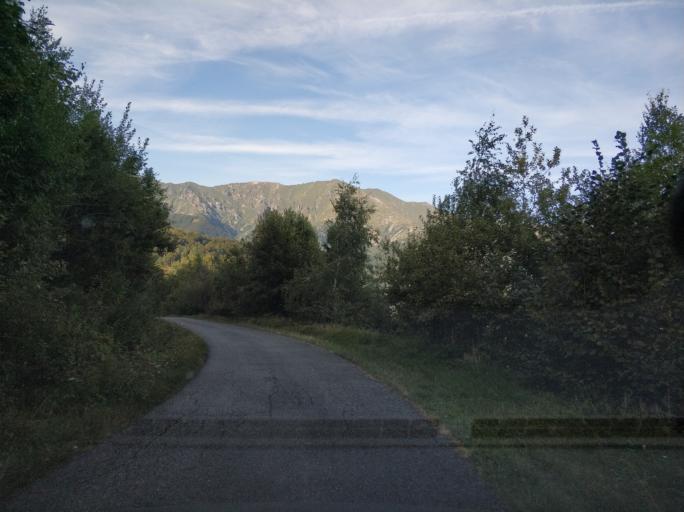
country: IT
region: Piedmont
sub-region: Provincia di Torino
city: Monastero di Lanzo
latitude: 45.3102
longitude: 7.4220
